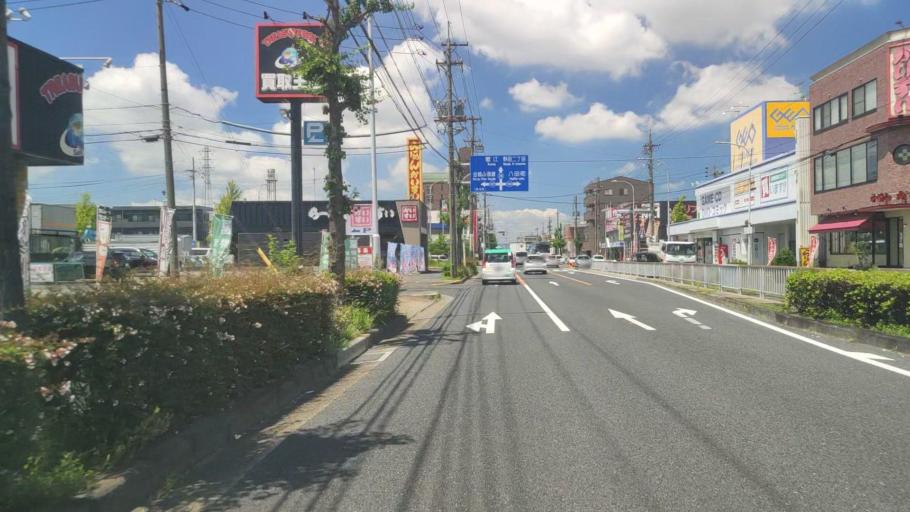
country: JP
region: Aichi
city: Kanie
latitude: 35.1404
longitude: 136.8453
